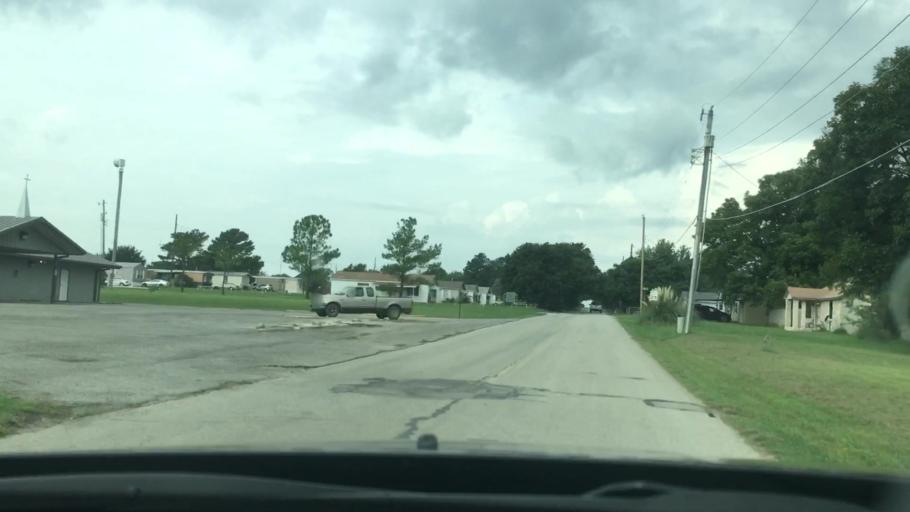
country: US
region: Oklahoma
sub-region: Carter County
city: Healdton
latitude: 34.2164
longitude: -97.4759
